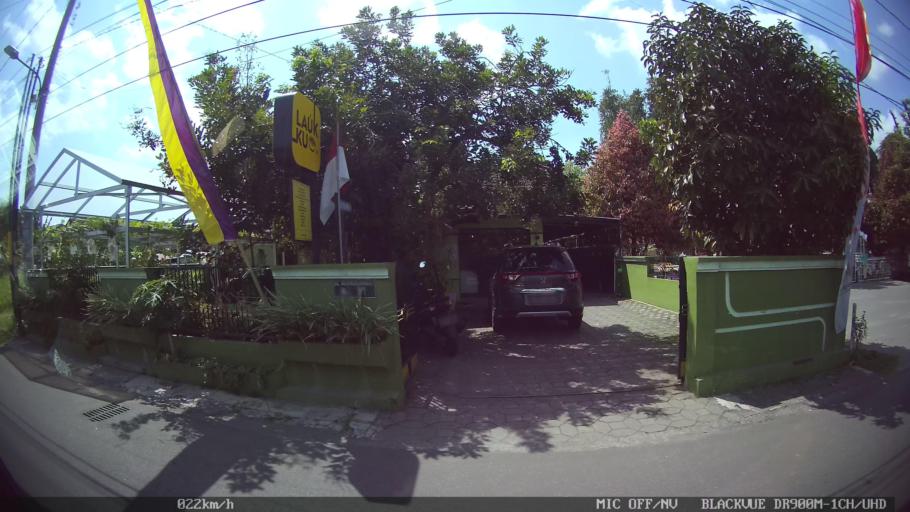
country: ID
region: Daerah Istimewa Yogyakarta
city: Yogyakarta
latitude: -7.8300
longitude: 110.3878
